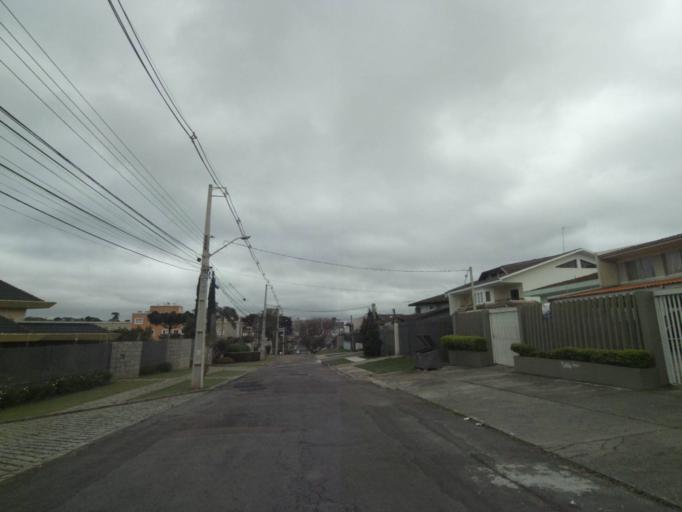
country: BR
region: Parana
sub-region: Curitiba
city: Curitiba
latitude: -25.4694
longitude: -49.2814
